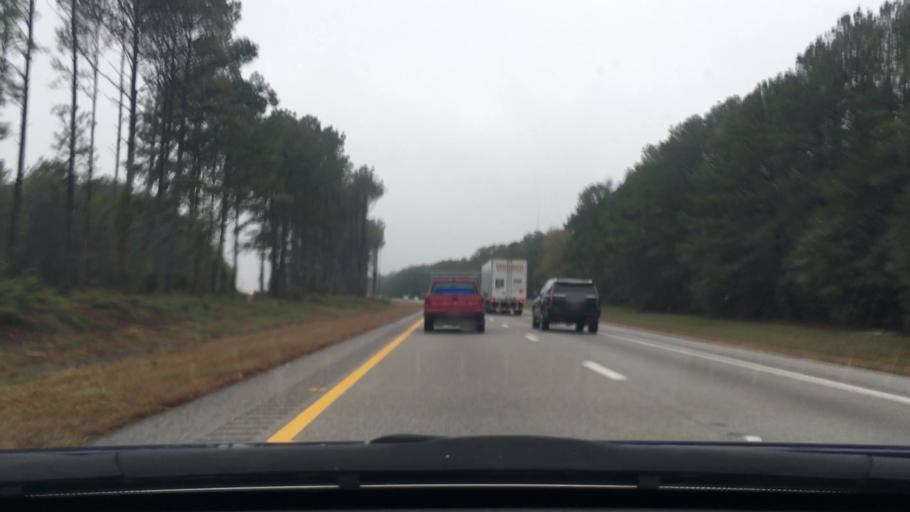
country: US
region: South Carolina
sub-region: Kershaw County
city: Camden
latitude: 34.2147
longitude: -80.5047
